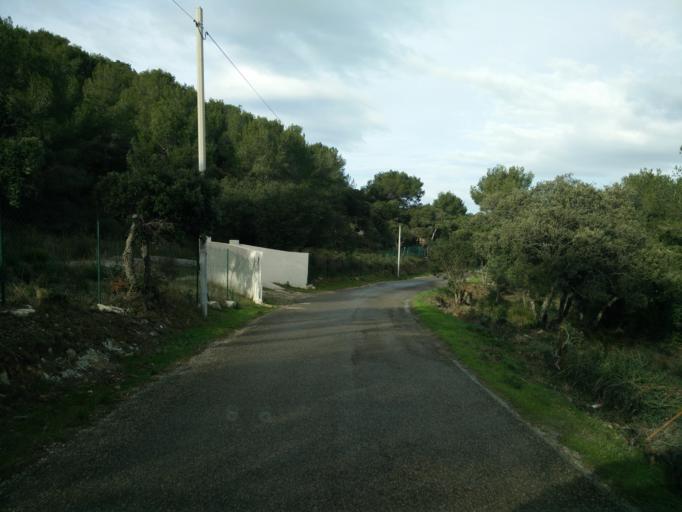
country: FR
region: Provence-Alpes-Cote d'Azur
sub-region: Departement du Var
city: Six-Fours-les-Plages
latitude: 43.0676
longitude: 5.8266
